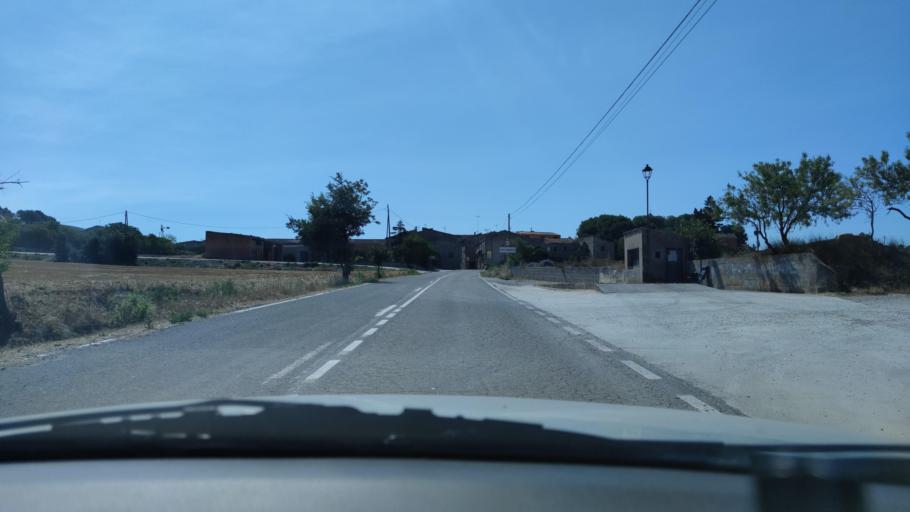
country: ES
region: Catalonia
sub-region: Provincia de Lleida
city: Sant Guim de Freixenet
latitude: 41.6202
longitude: 1.3517
